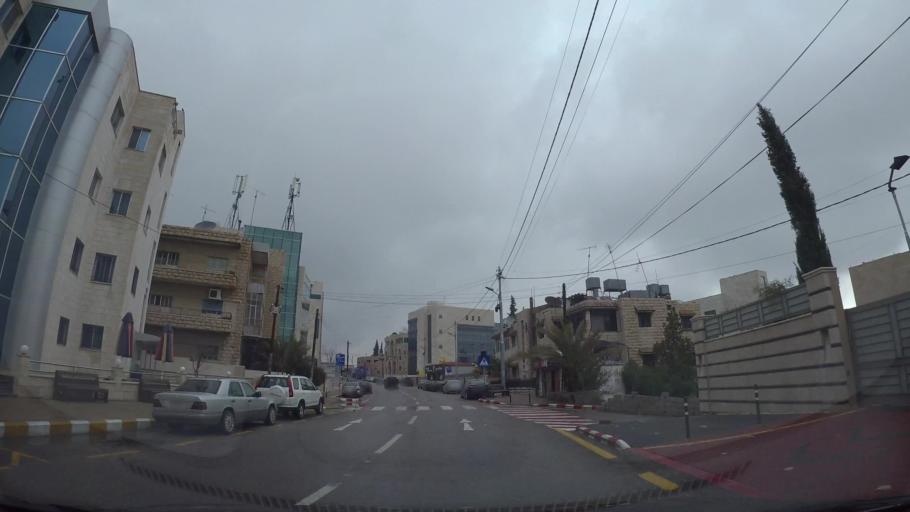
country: JO
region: Amman
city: Amman
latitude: 31.9502
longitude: 35.9073
